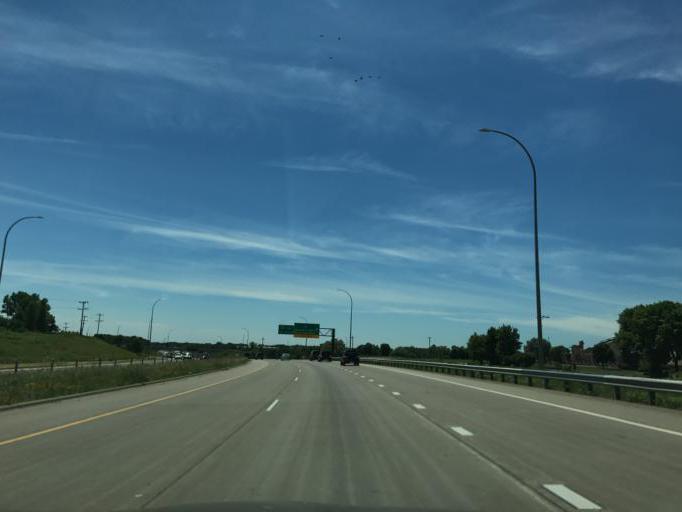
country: US
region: Minnesota
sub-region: Hennepin County
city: Osseo
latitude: 45.0997
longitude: -93.4020
